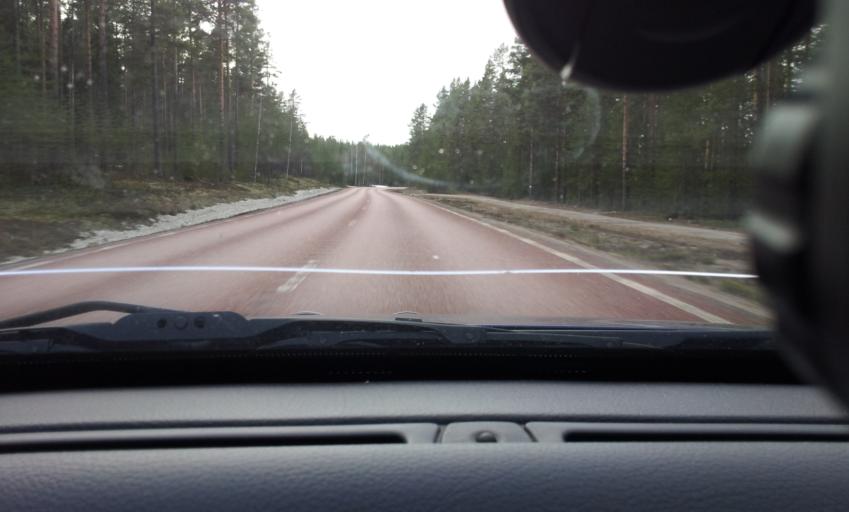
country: SE
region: Gaevleborg
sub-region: Ljusdals Kommun
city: Farila
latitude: 61.8996
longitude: 15.6479
